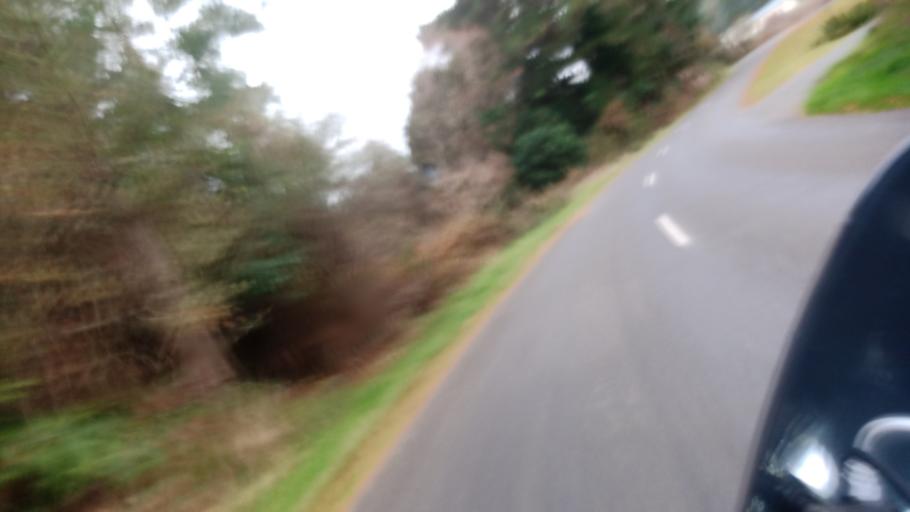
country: NZ
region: Bay of Plenty
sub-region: Whakatane District
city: Murupara
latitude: -38.5886
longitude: 176.7763
